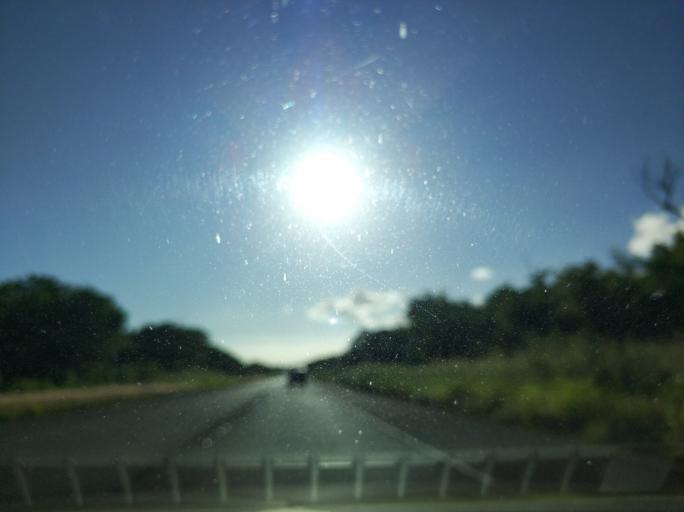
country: US
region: Hawaii
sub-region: Hawaii County
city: Leilani Estates
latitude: 19.3658
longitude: -154.9691
